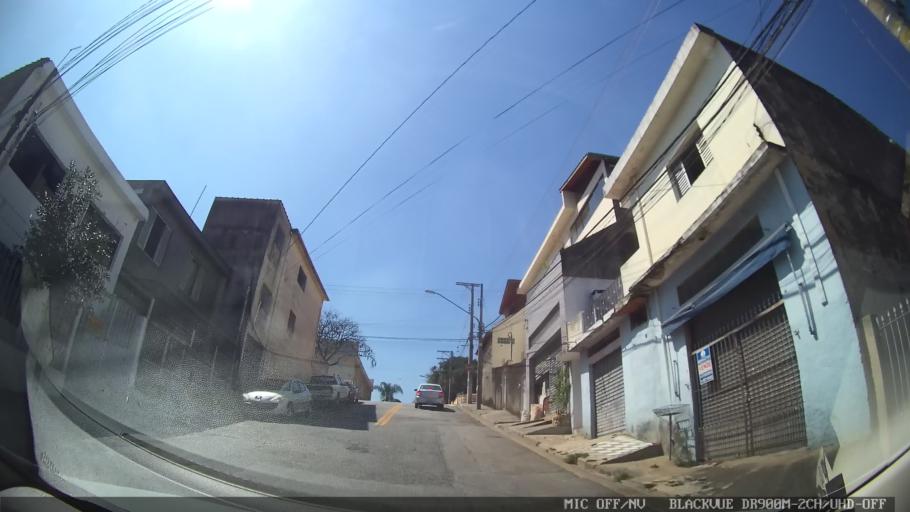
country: BR
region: Sao Paulo
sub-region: Sao Paulo
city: Sao Paulo
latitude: -23.4971
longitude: -46.6569
